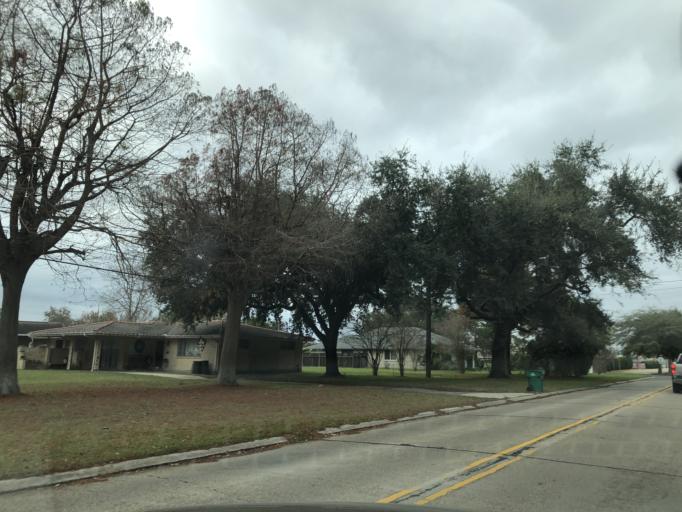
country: US
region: Louisiana
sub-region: Jefferson Parish
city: Metairie
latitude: 29.9885
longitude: -90.1600
